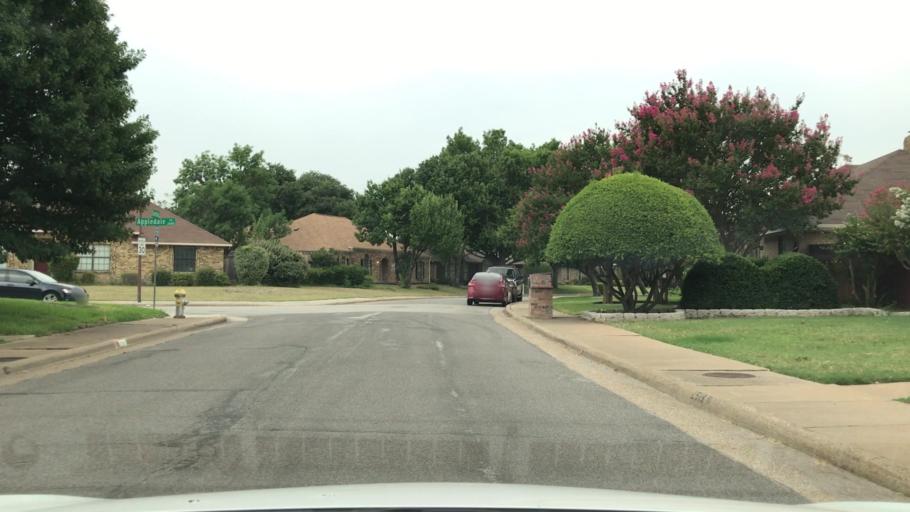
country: US
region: Texas
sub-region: Dallas County
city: Carrollton
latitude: 32.9953
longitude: -96.8694
